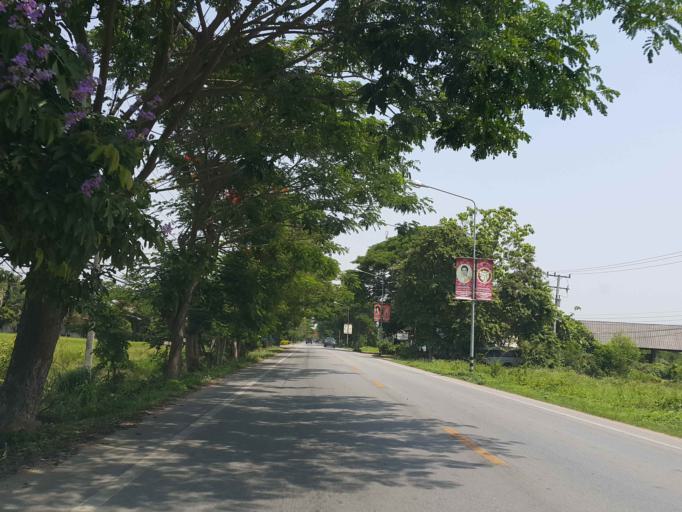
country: TH
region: Chiang Mai
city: Mae Taeng
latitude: 19.0260
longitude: 98.9680
